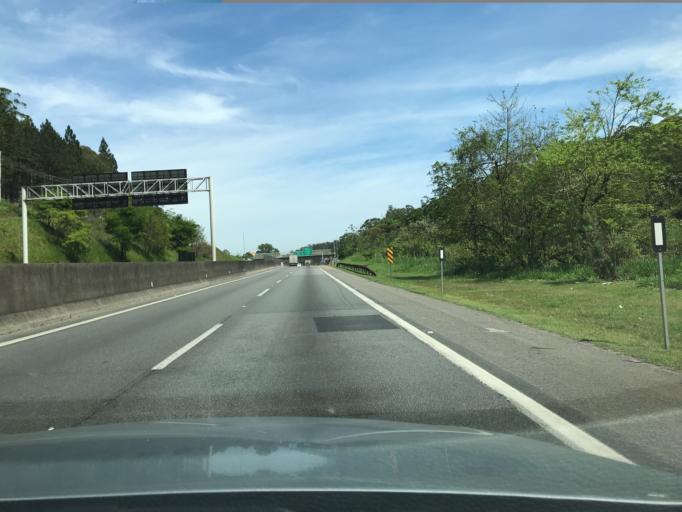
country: BR
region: Sao Paulo
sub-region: Caieiras
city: Caieiras
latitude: -23.4155
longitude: -46.8040
